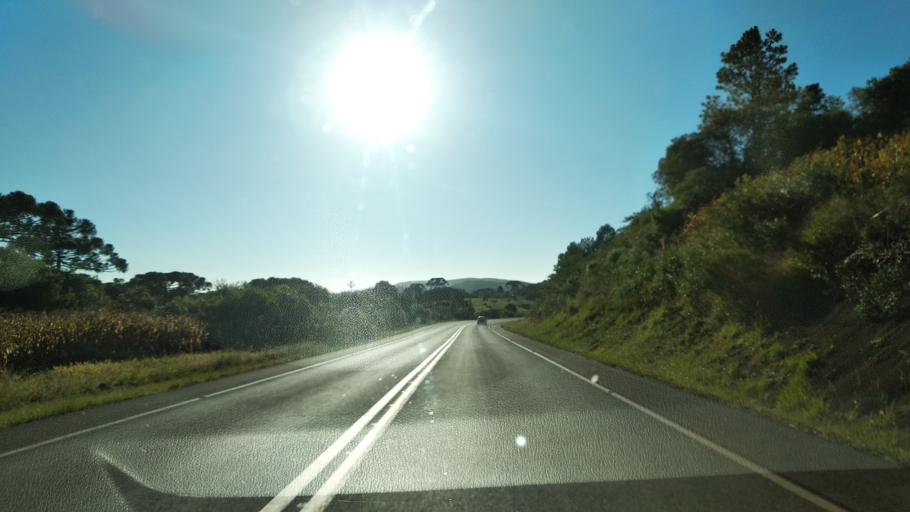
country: BR
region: Santa Catarina
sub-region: Lages
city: Lages
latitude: -27.7853
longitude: -50.4496
